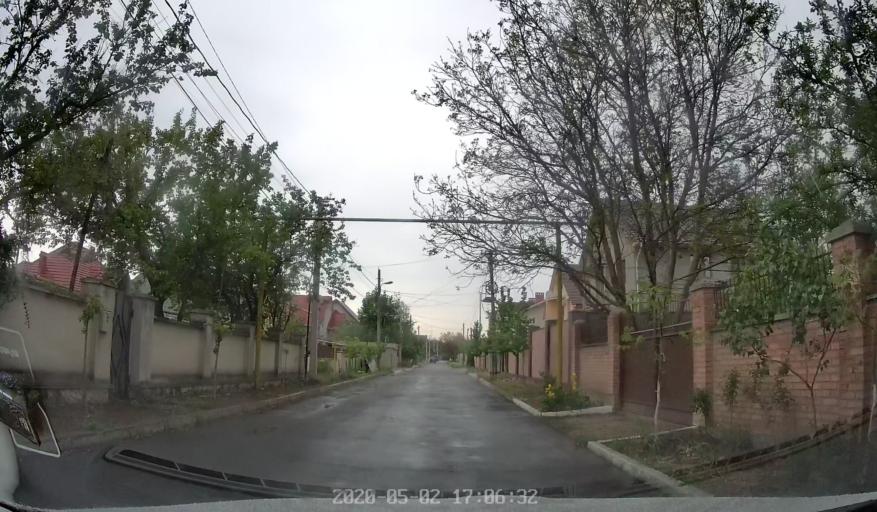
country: MD
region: Chisinau
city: Chisinau
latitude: 46.9700
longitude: 28.8320
